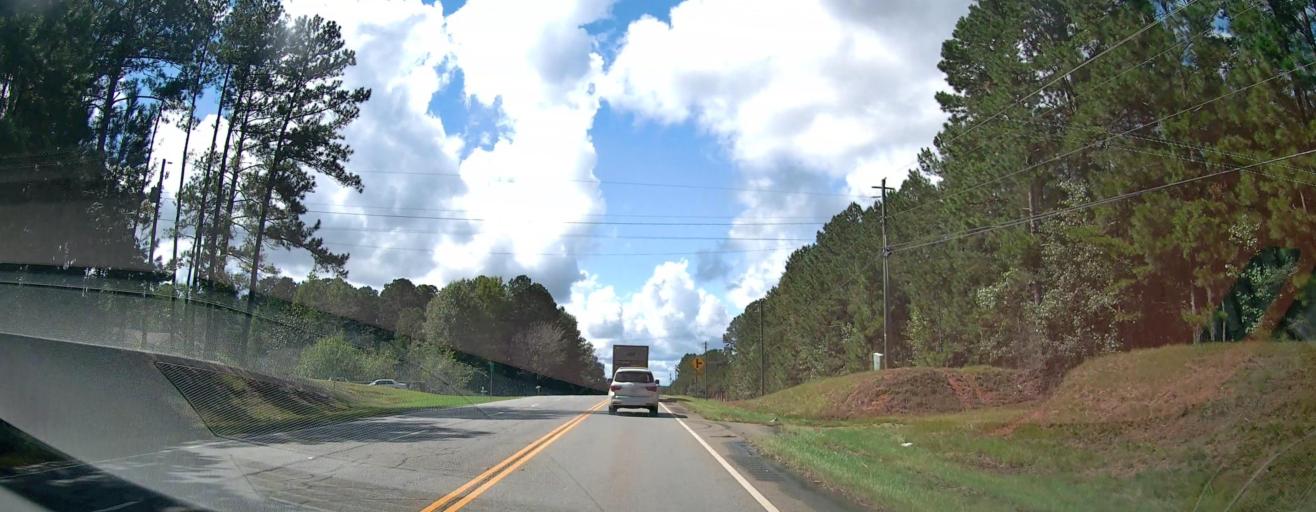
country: US
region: Georgia
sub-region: Jones County
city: Gray
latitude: 33.0281
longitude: -83.4522
